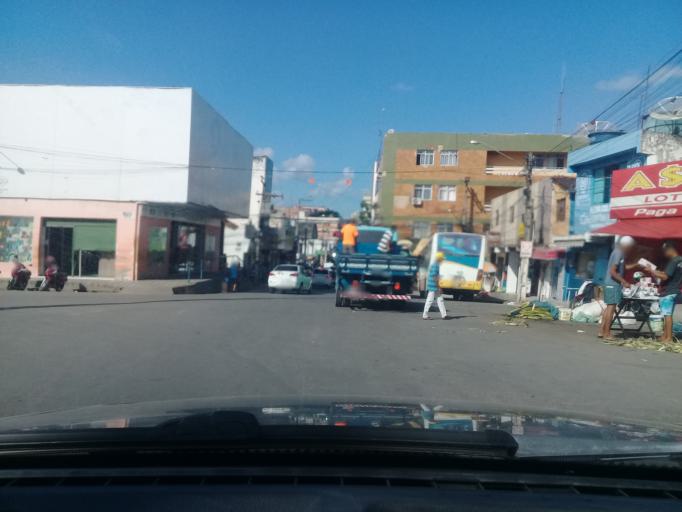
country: BR
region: Pernambuco
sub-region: Vitoria De Santo Antao
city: Vitoria de Santo Antao
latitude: -8.1205
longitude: -35.2967
